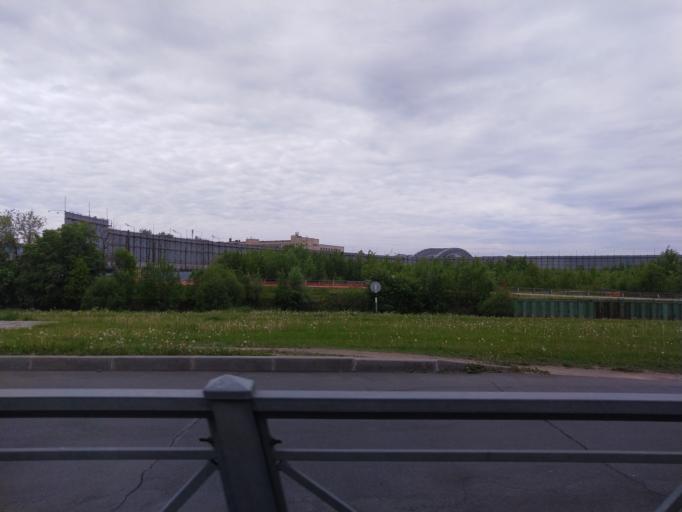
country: RU
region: St.-Petersburg
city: Centralniy
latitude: 59.9436
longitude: 30.4111
